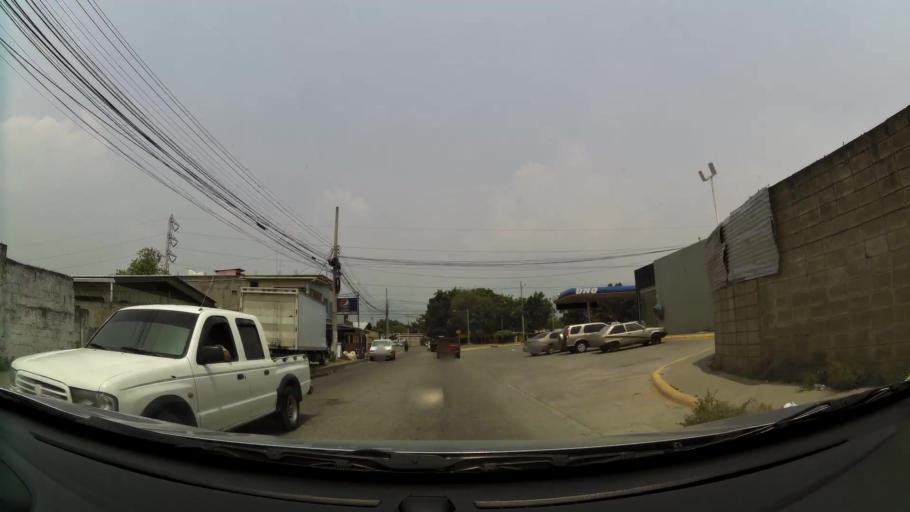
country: HN
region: Cortes
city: San Pedro Sula
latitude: 15.4927
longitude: -88.0046
